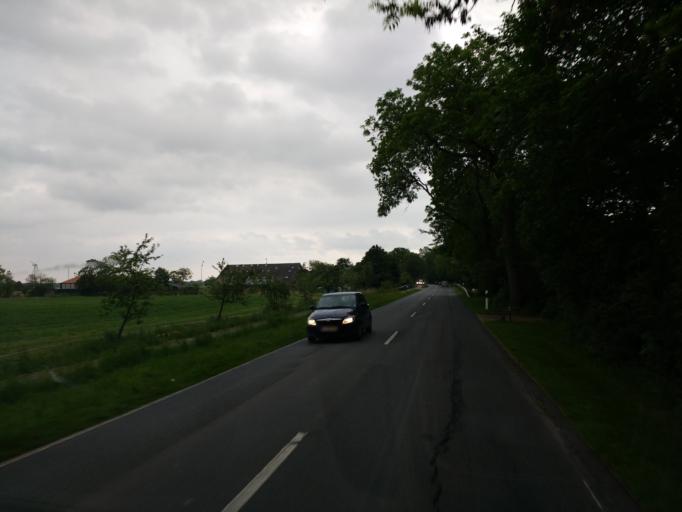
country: DE
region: Lower Saxony
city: Schillig
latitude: 53.6466
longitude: 7.9979
